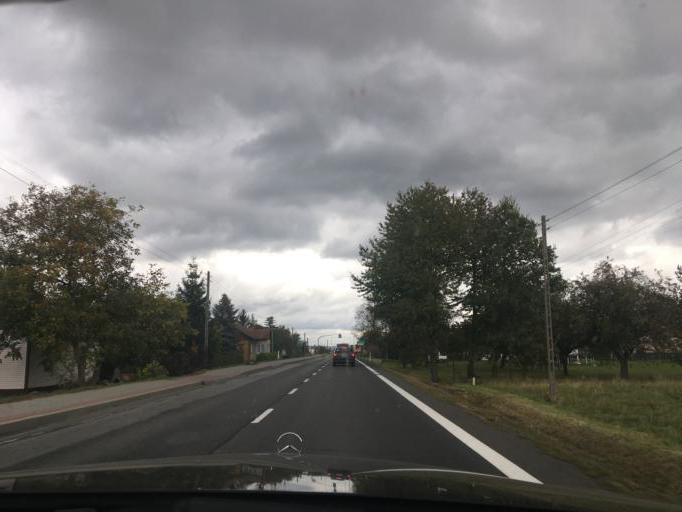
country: PL
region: Subcarpathian Voivodeship
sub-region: Powiat krosnienski
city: Miejsce Piastowe
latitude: 49.6492
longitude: 21.8164
